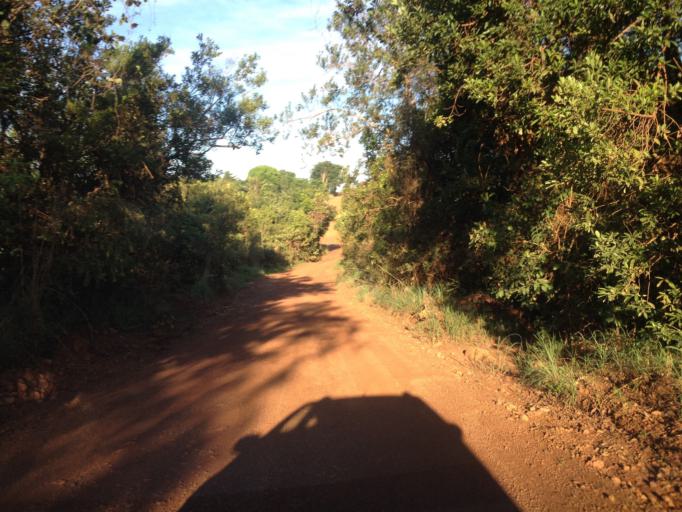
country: BR
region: Goias
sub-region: Abadiania
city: Abadiania
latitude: -15.9988
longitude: -48.5478
